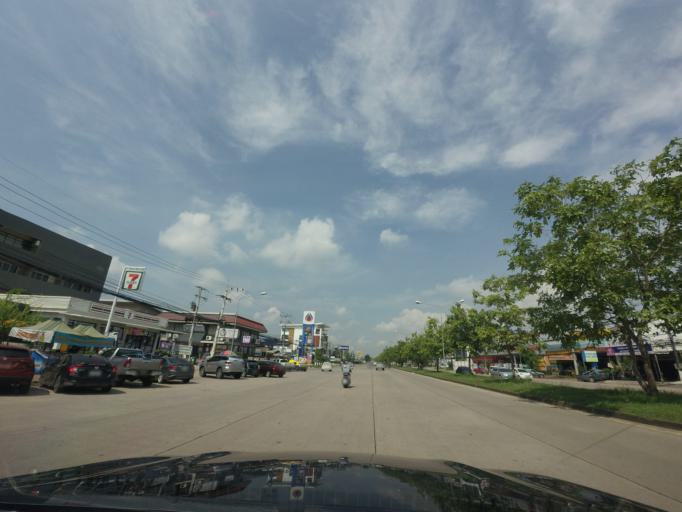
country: TH
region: Khon Kaen
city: Khon Kaen
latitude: 16.4424
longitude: 102.8087
